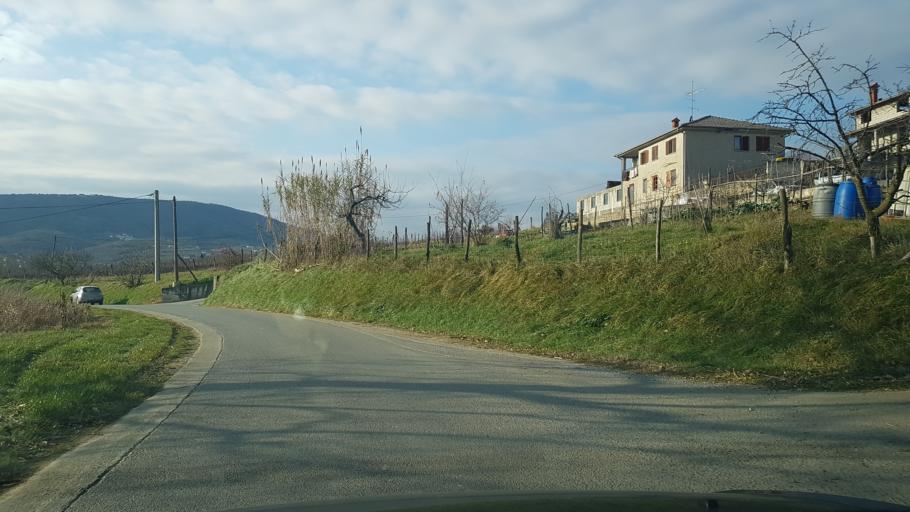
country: SI
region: Koper-Capodistria
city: Prade
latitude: 45.5292
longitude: 13.7757
